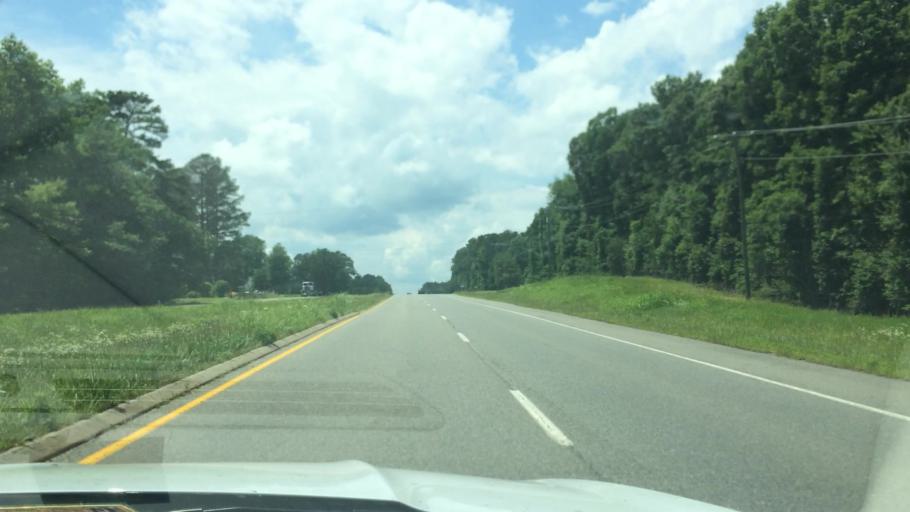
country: US
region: Virginia
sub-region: Middlesex County
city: Saluda
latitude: 37.5625
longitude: -76.6295
